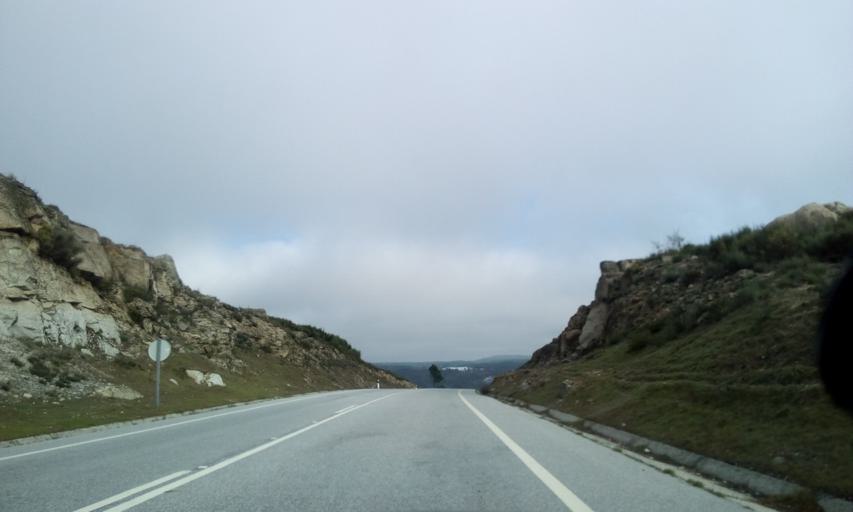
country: PT
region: Guarda
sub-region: Aguiar da Beira
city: Aguiar da Beira
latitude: 40.7674
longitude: -7.5030
